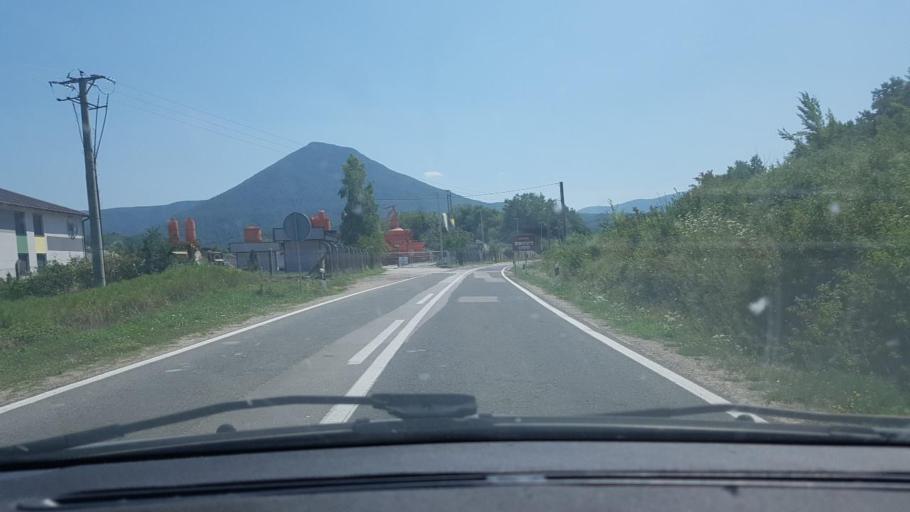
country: BA
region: Federation of Bosnia and Herzegovina
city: Bihac
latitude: 44.7648
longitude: 15.9448
